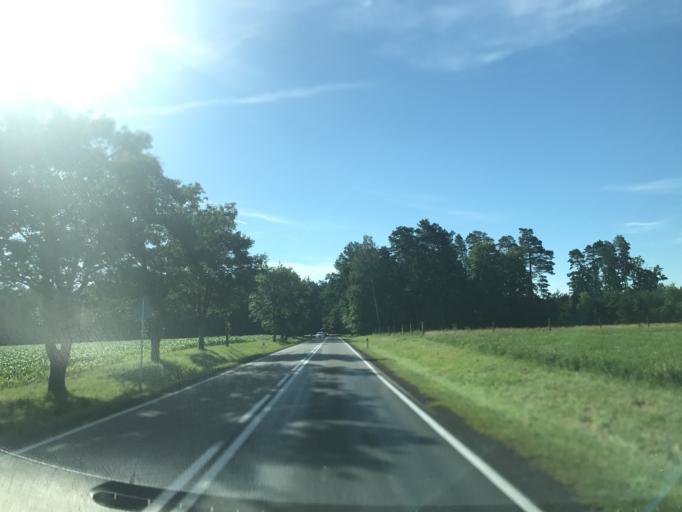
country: PL
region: Pomeranian Voivodeship
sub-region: Powiat czluchowski
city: Przechlewo
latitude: 53.7047
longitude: 17.2680
